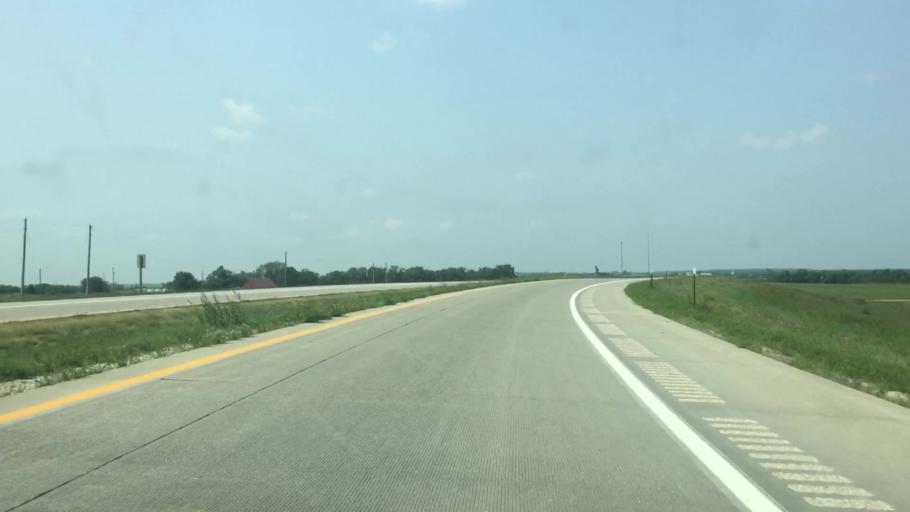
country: US
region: Kansas
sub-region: Franklin County
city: Ottawa
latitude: 38.6358
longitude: -95.2205
